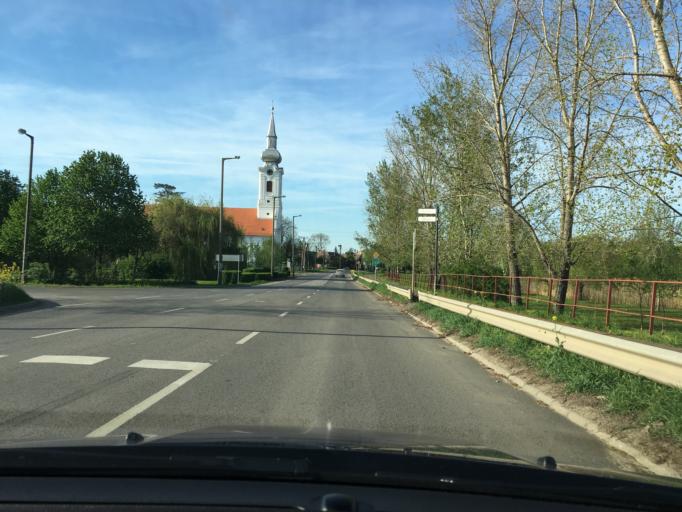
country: HU
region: Bekes
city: Korosladany
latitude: 46.9551
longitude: 21.0819
